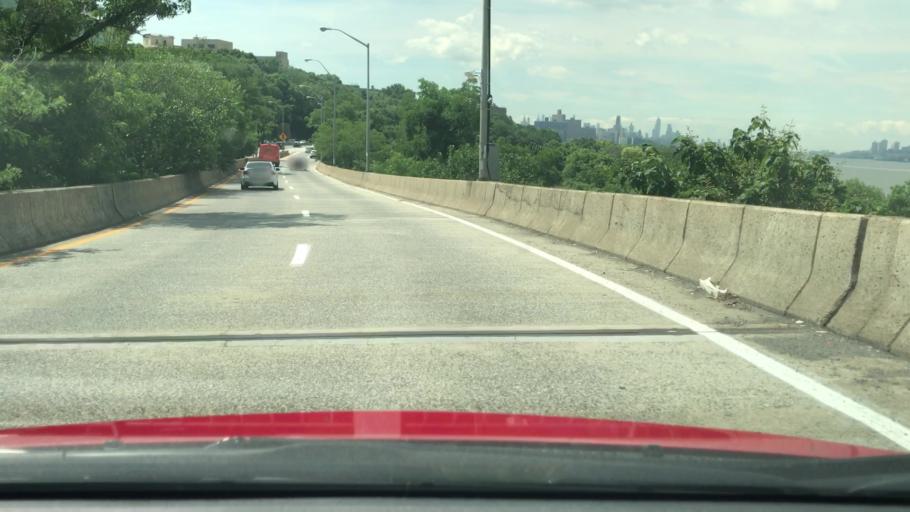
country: US
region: New Jersey
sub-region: Bergen County
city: Fort Lee
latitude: 40.8456
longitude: -73.9468
